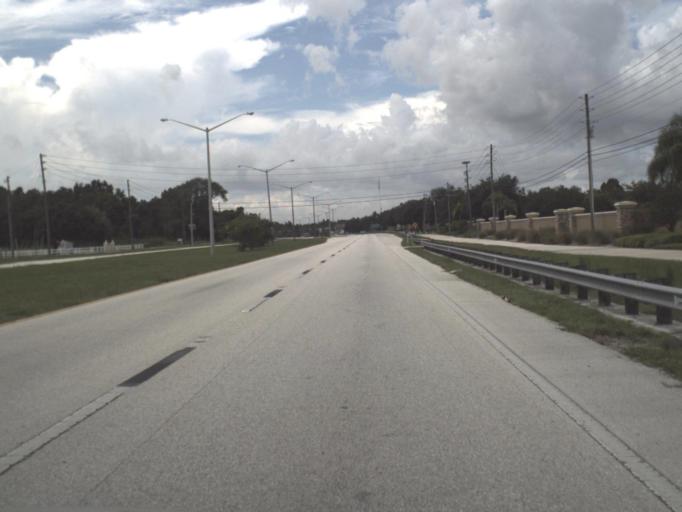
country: US
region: Florida
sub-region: Pinellas County
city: East Lake
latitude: 28.1338
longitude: -82.6970
